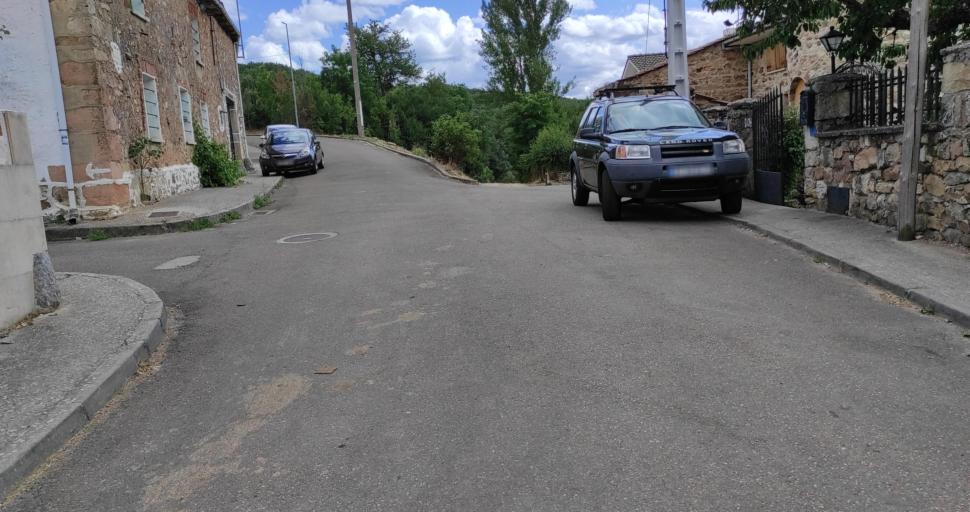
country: ES
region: Castille and Leon
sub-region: Provincia de Leon
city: Valdepielago
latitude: 42.8559
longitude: -5.3954
